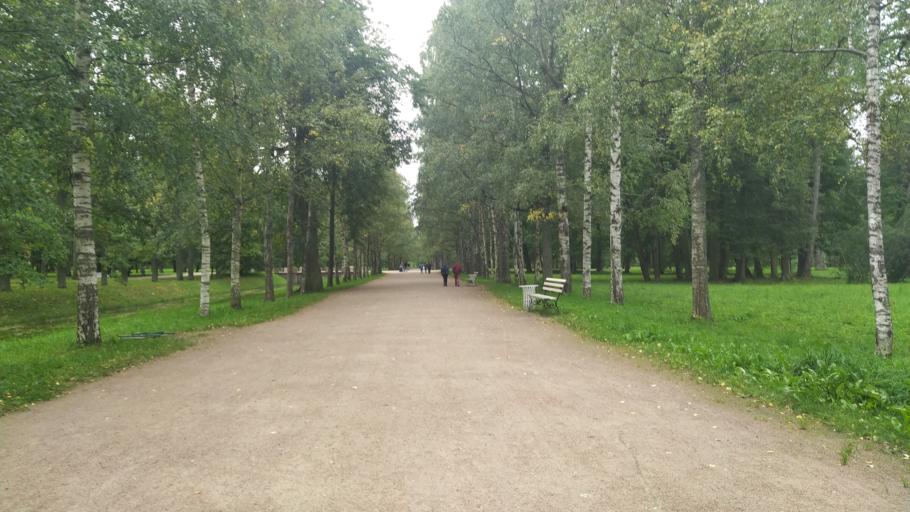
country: RU
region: St.-Petersburg
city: Pushkin
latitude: 59.7201
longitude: 30.3865
